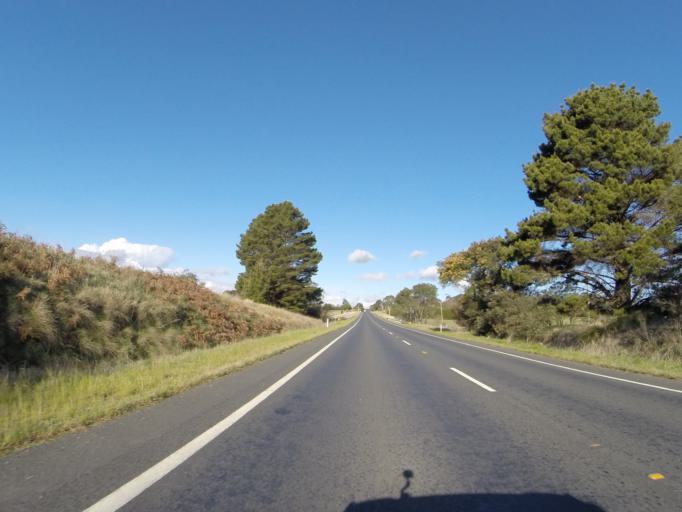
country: AU
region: New South Wales
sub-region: Wingecarribee
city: Moss Vale
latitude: -34.5714
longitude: 150.4527
